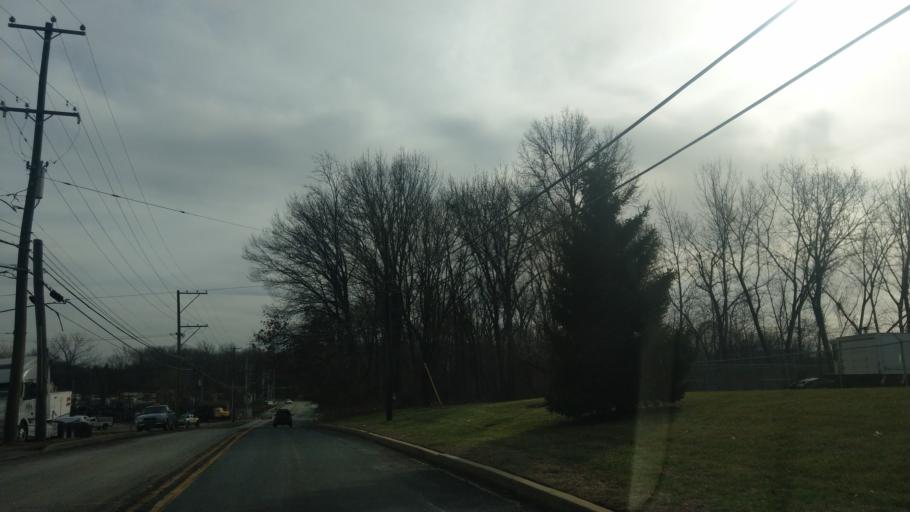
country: US
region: Pennsylvania
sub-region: Bucks County
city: Eddington
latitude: 40.0783
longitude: -74.9307
